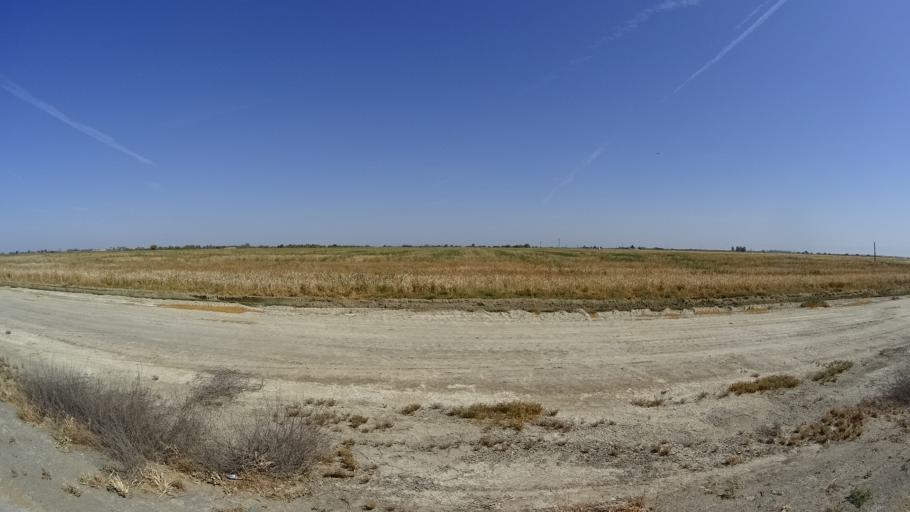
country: US
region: California
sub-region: Kings County
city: Stratford
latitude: 36.2111
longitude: -119.7334
